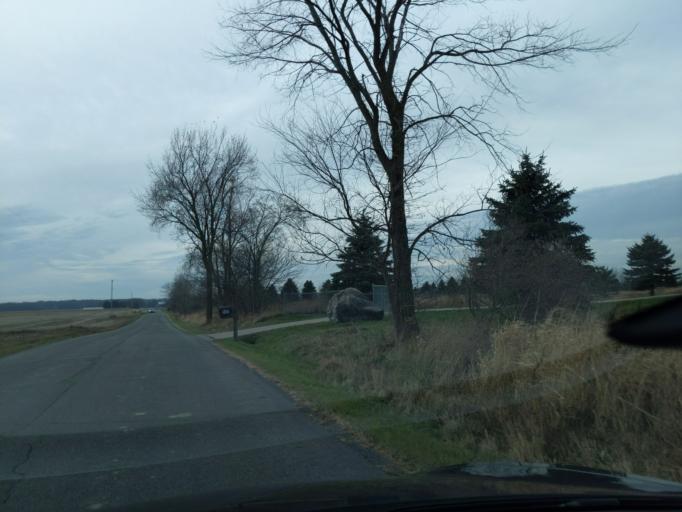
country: US
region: Michigan
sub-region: Ingham County
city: Okemos
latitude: 42.6545
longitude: -84.3755
